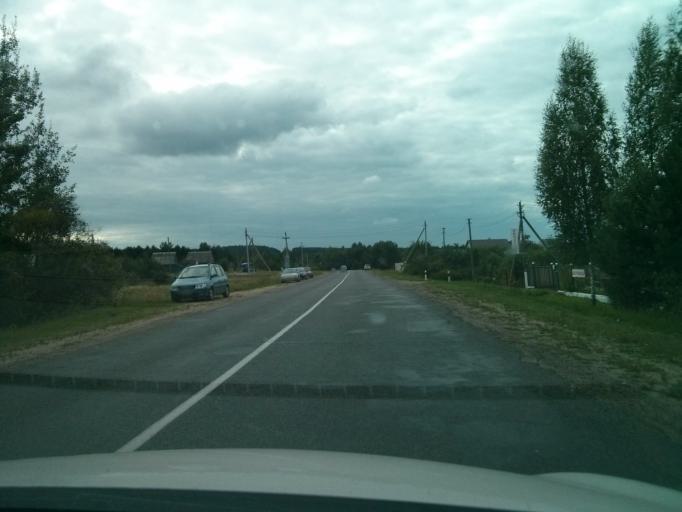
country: BY
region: Minsk
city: Horad Barysaw
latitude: 54.2864
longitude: 28.5471
